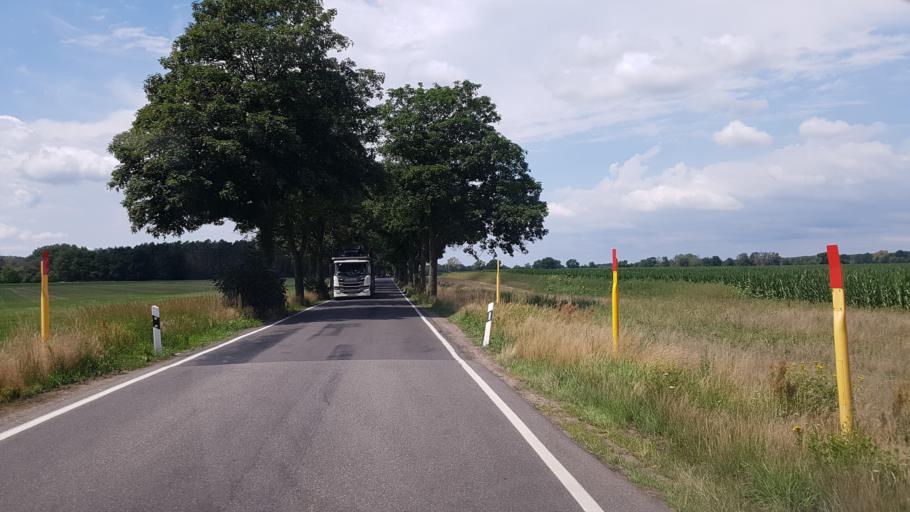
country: DE
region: Brandenburg
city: Senftenberg
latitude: 51.4878
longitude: 14.0868
